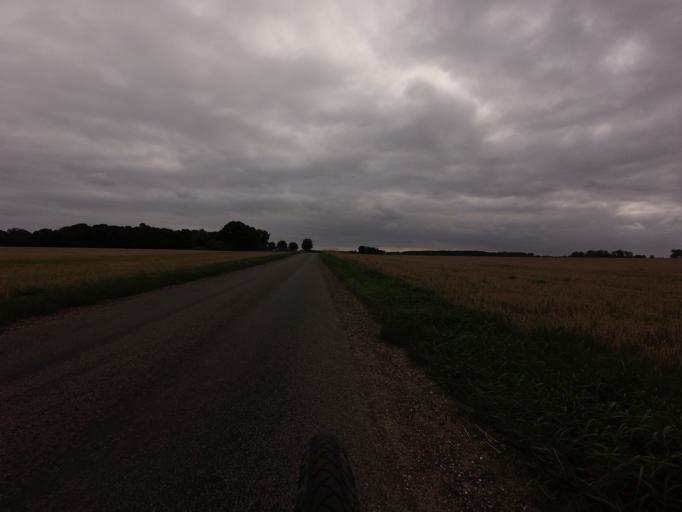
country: DK
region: Zealand
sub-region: Stevns Kommune
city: Store Heddinge
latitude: 55.3327
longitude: 12.3307
